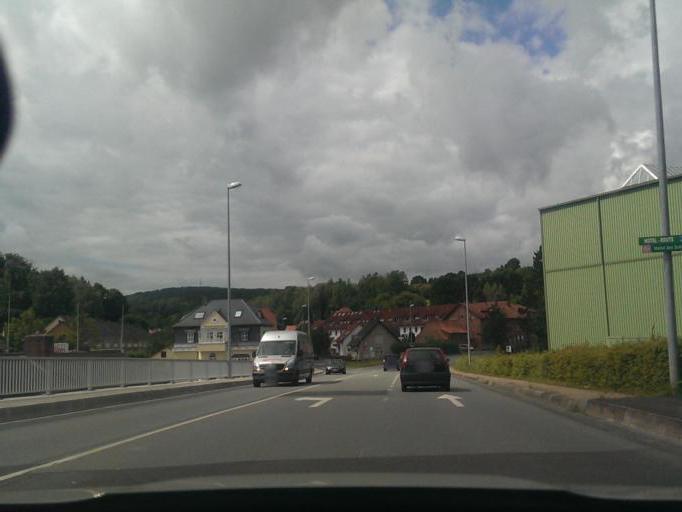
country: DE
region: Lower Saxony
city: Alfeld
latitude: 51.9791
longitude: 9.8202
